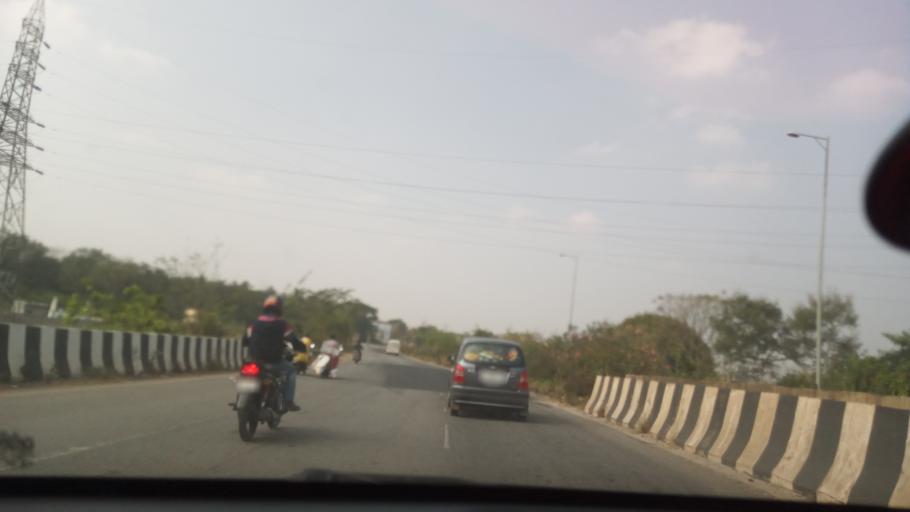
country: IN
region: Karnataka
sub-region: Mysore
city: Nanjangud
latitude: 12.1966
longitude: 76.6663
